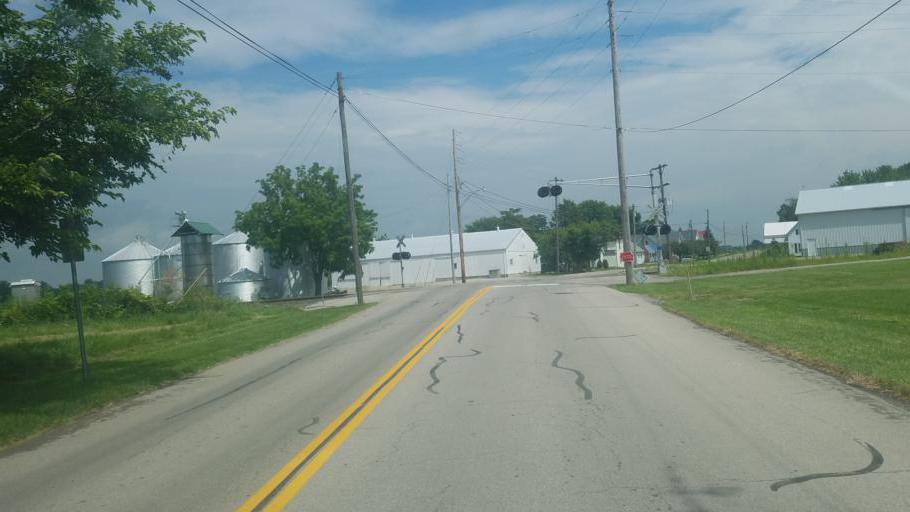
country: US
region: Ohio
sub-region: Champaign County
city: North Lewisburg
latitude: 40.4027
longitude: -83.5410
